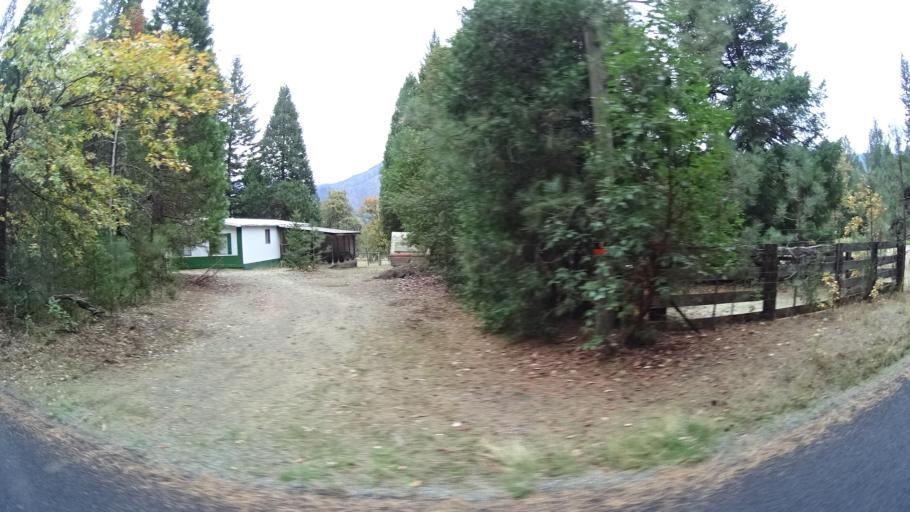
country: US
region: California
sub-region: Siskiyou County
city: Happy Camp
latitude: 41.8480
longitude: -123.1899
